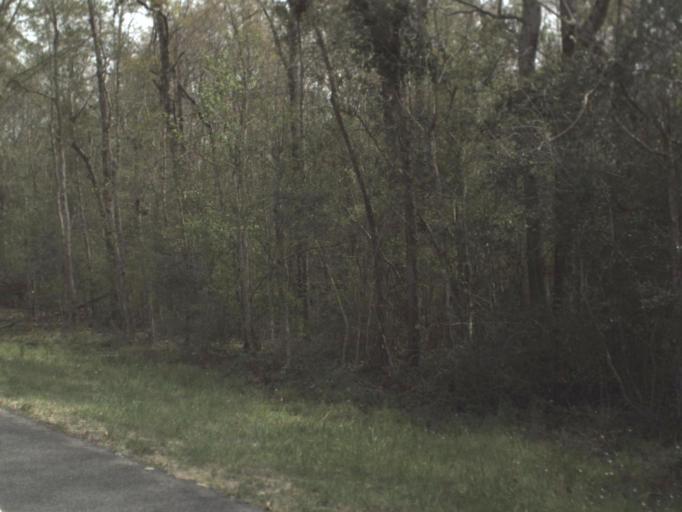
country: US
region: Alabama
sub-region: Geneva County
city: Geneva
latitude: 30.9498
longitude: -85.9325
